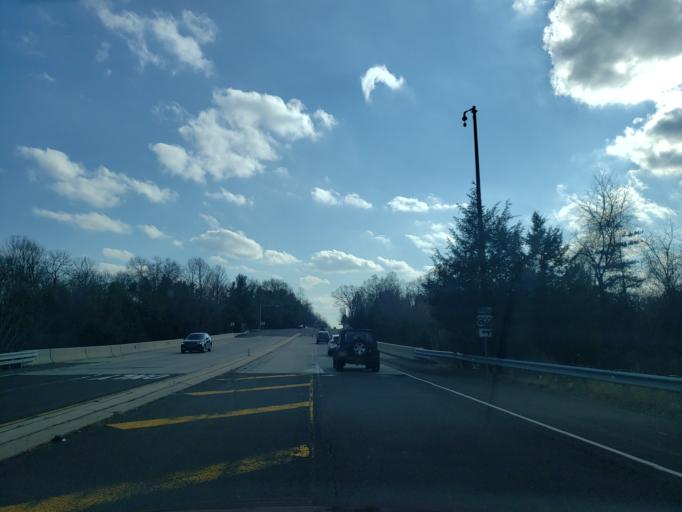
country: US
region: Pennsylvania
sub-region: Bucks County
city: Doylestown
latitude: 40.2995
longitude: -75.1282
